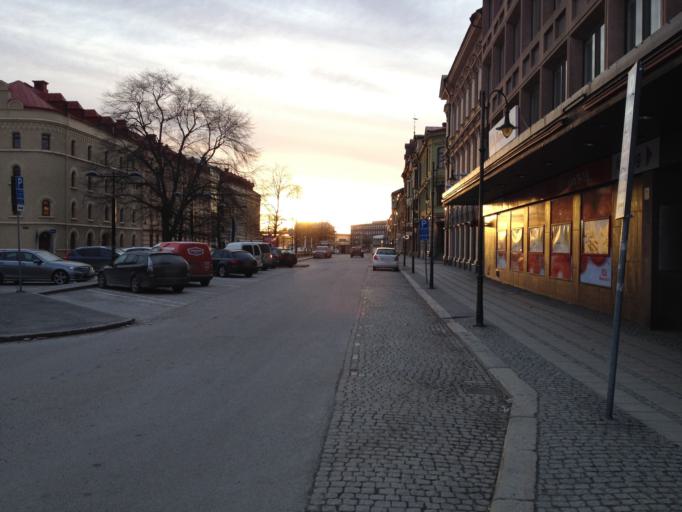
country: SE
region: Vaesternorrland
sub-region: Sundsvalls Kommun
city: Sundsvall
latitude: 62.3916
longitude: 17.3095
